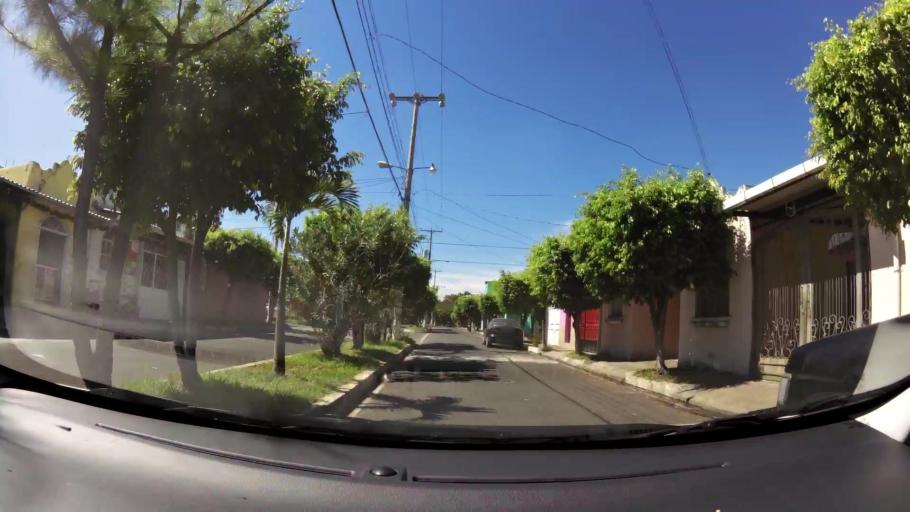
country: SV
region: La Libertad
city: San Juan Opico
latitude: 13.7960
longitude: -89.3589
